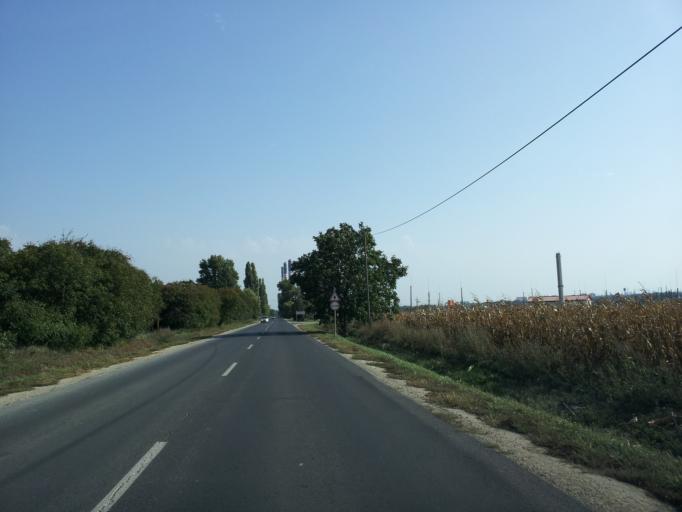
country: HU
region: Pest
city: Szazhalombatta
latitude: 47.3466
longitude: 18.9049
